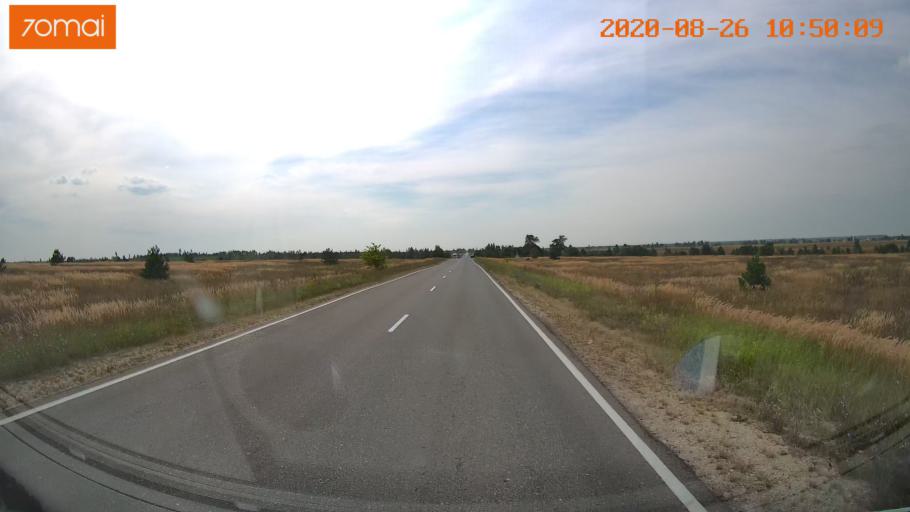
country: RU
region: Rjazan
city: Lashma
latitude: 54.6915
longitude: 41.1571
